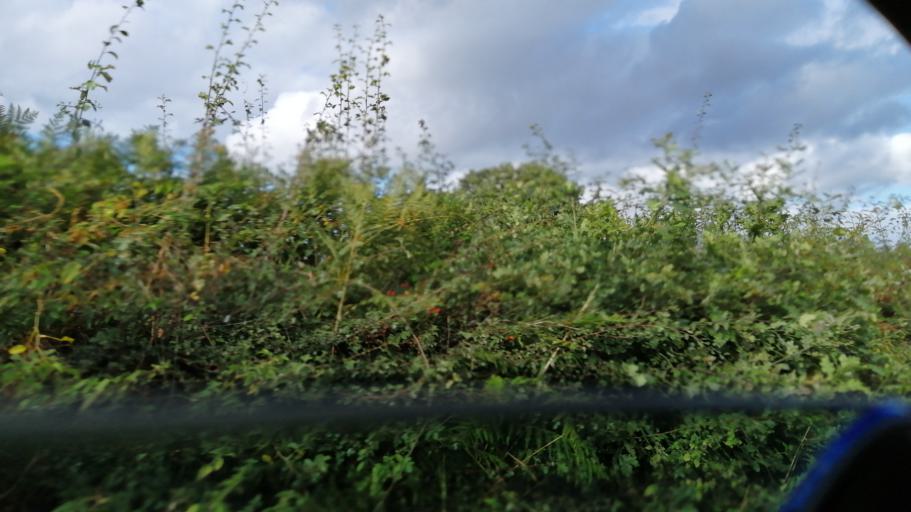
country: GB
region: England
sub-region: Herefordshire
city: Callow
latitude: 52.0096
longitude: -2.7534
